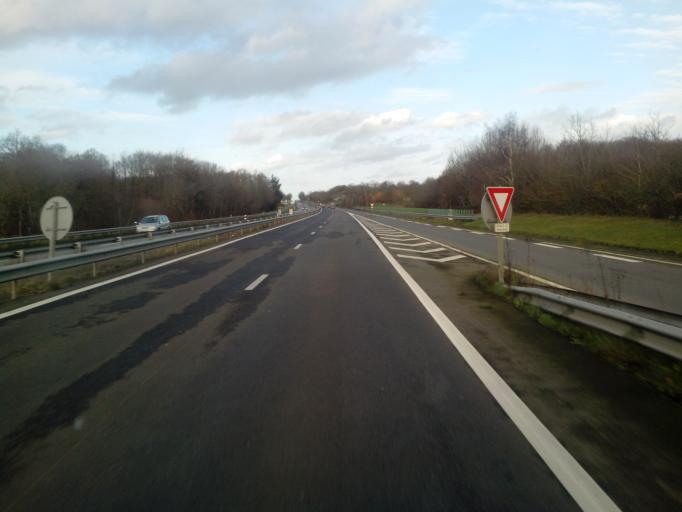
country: FR
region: Brittany
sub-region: Departement d'Ille-et-Vilaine
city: Saint-Pierre-de-Plesguen
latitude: 48.4641
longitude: -1.9146
